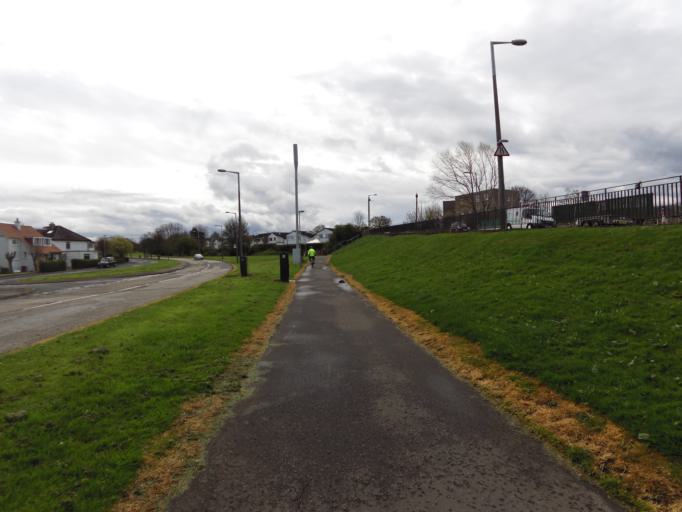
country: GB
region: Scotland
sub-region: Edinburgh
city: Colinton
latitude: 55.9673
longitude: -3.2686
